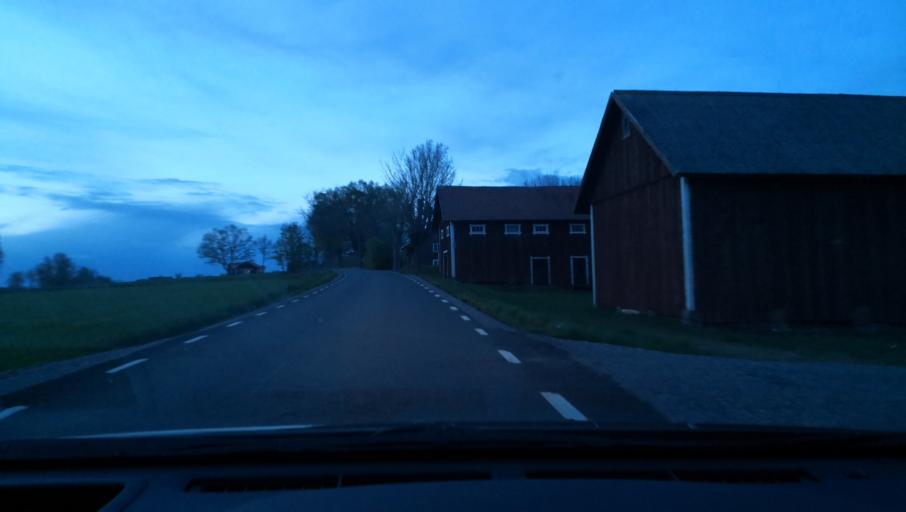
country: SE
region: OErebro
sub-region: Askersunds Kommun
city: Asbro
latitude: 59.0485
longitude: 14.9291
